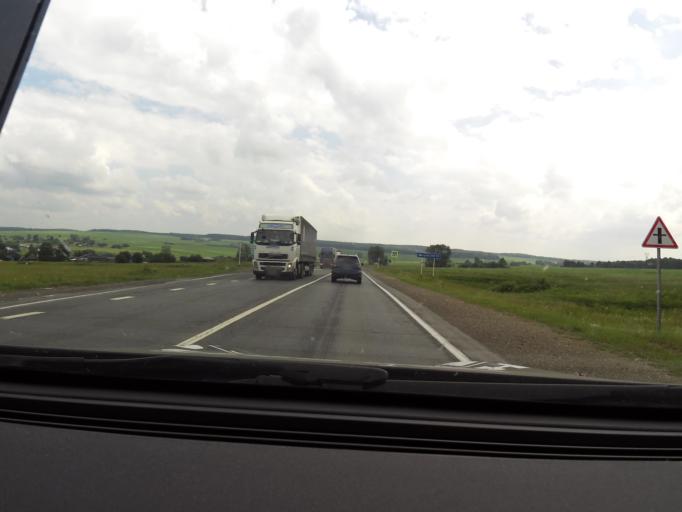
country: RU
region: Sverdlovsk
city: Achit
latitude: 56.8965
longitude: 57.6025
